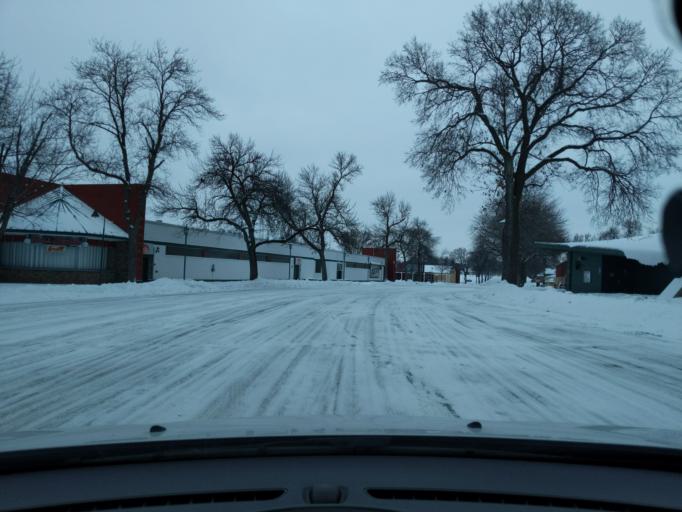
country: US
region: Minnesota
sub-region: Ramsey County
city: Falcon Heights
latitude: 44.9798
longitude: -93.1690
